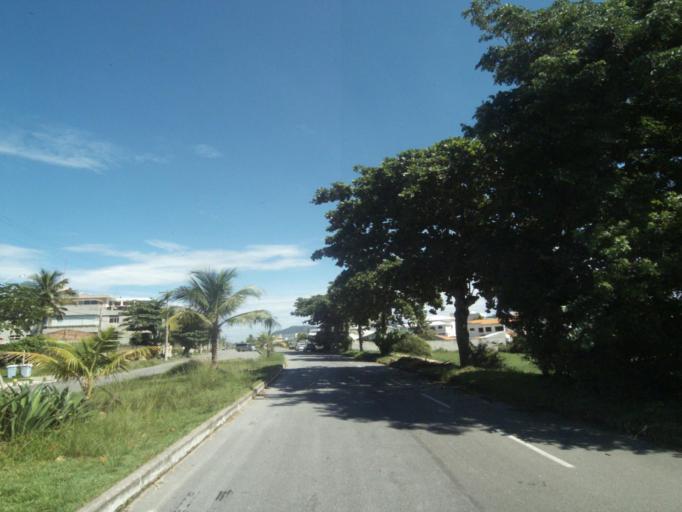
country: BR
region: Rio de Janeiro
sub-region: Niteroi
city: Niteroi
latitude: -22.9615
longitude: -43.0532
